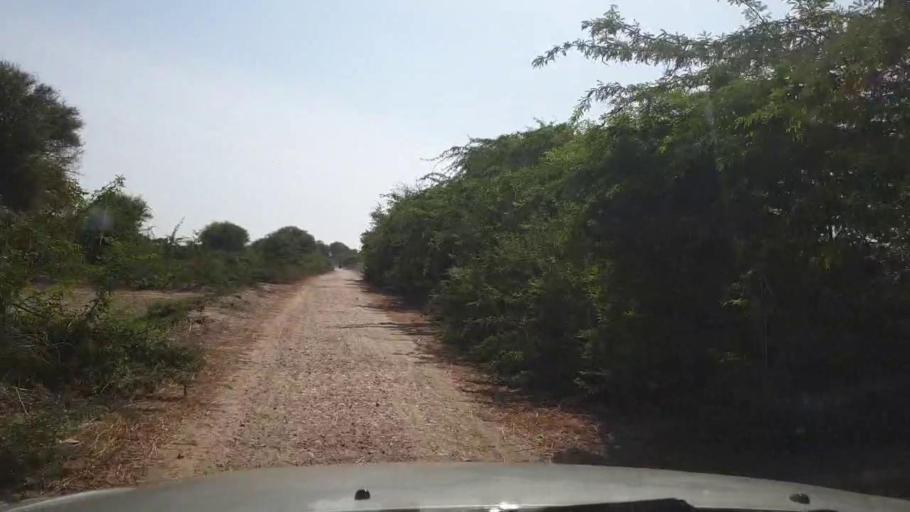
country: PK
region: Sindh
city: Bulri
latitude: 24.9563
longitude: 68.3256
